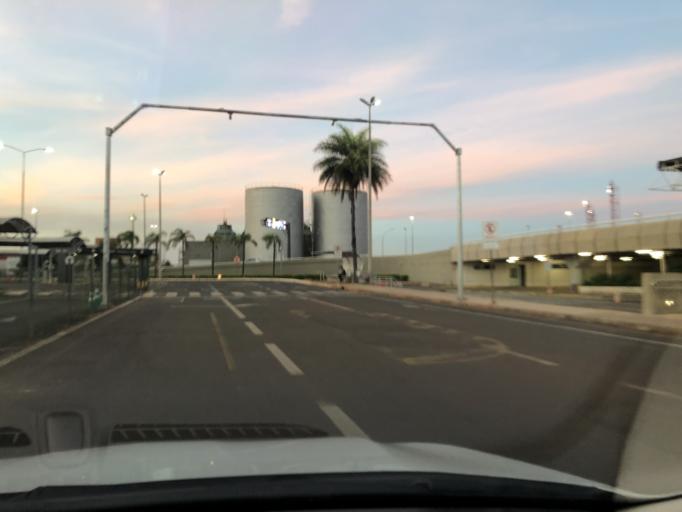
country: BR
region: Federal District
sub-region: Brasilia
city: Brasilia
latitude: -15.8697
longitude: -47.9220
